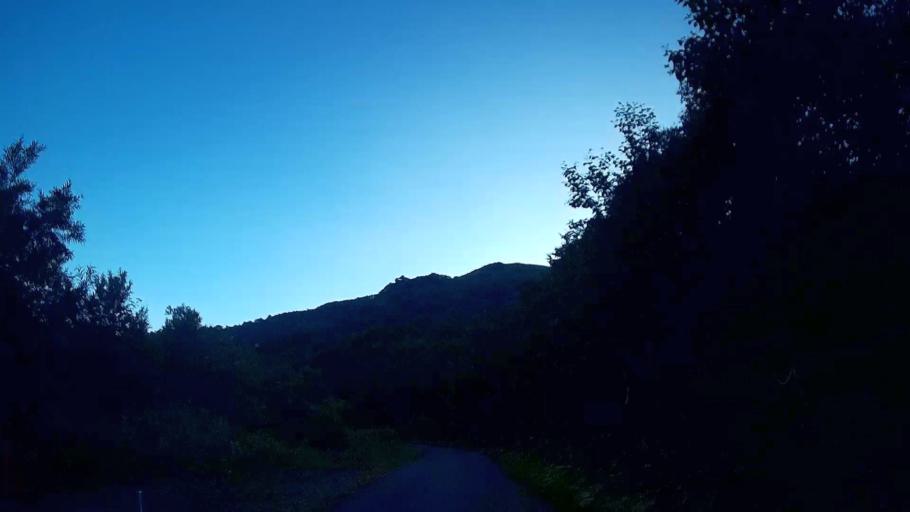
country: JP
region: Hokkaido
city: Iwanai
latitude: 42.5984
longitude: 139.9602
